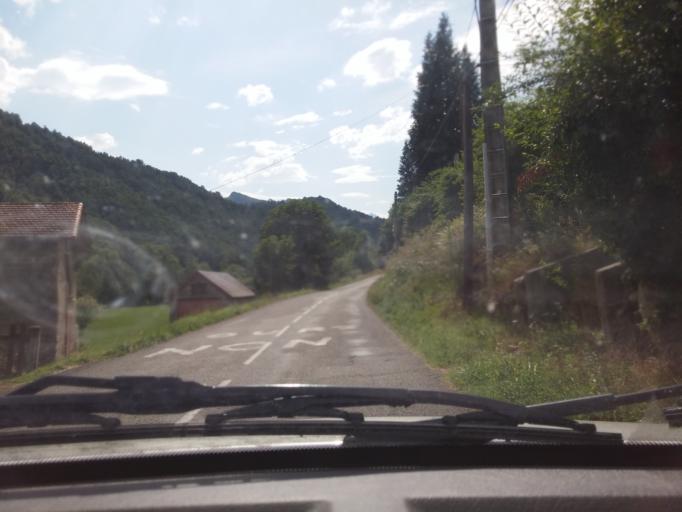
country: FR
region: Midi-Pyrenees
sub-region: Departement de l'Ariege
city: Saint-Girons
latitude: 42.8612
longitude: 1.2567
